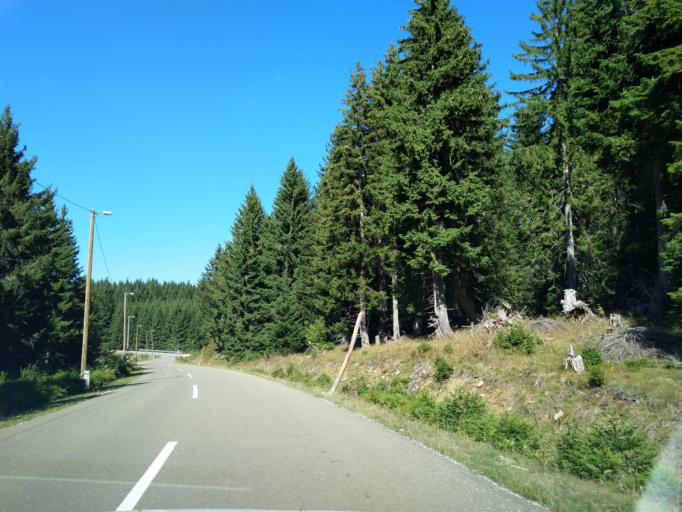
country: RS
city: Sokolovica
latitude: 43.2734
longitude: 20.3483
